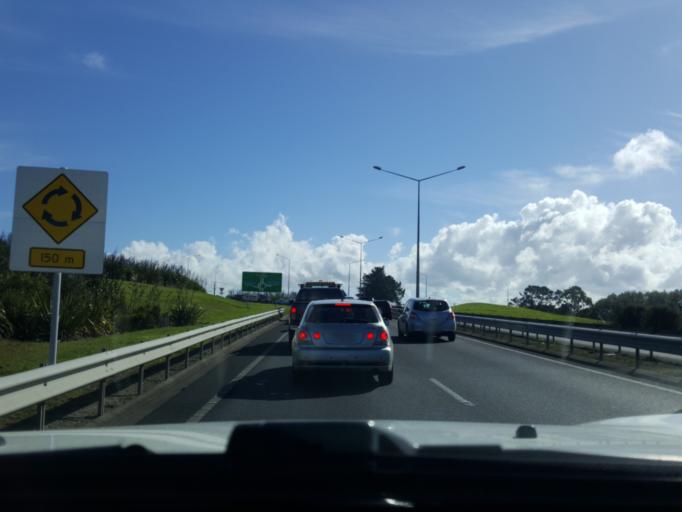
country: NZ
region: Auckland
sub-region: Auckland
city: Rosebank
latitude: -36.7985
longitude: 174.5986
